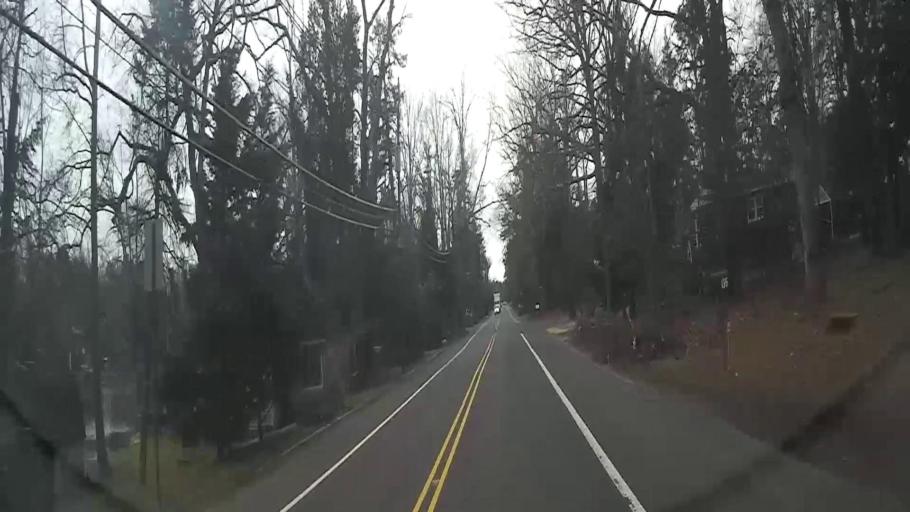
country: US
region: New Jersey
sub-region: Burlington County
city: Medford Lakes
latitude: 39.8605
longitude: -74.8537
